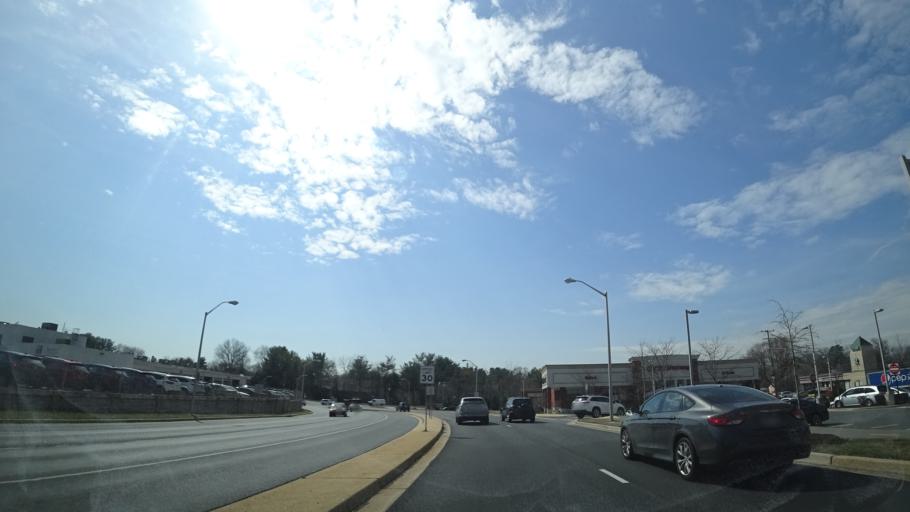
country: US
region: Maryland
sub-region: Montgomery County
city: Rockville
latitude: 39.0769
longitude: -77.1398
